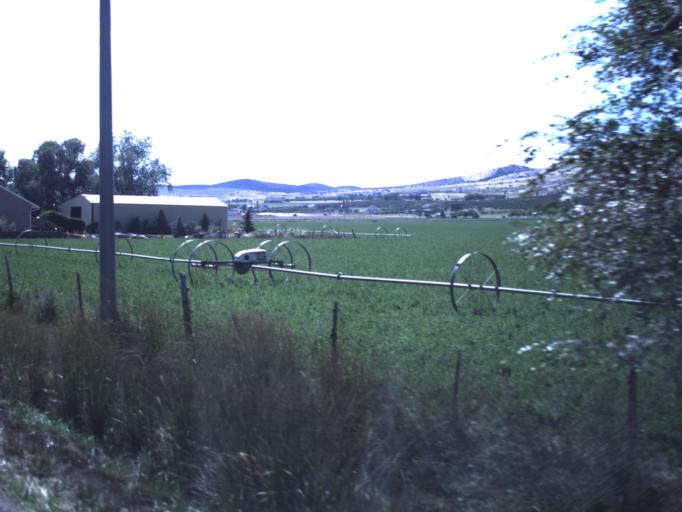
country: US
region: Utah
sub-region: Utah County
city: West Mountain
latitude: 40.0613
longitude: -111.7876
